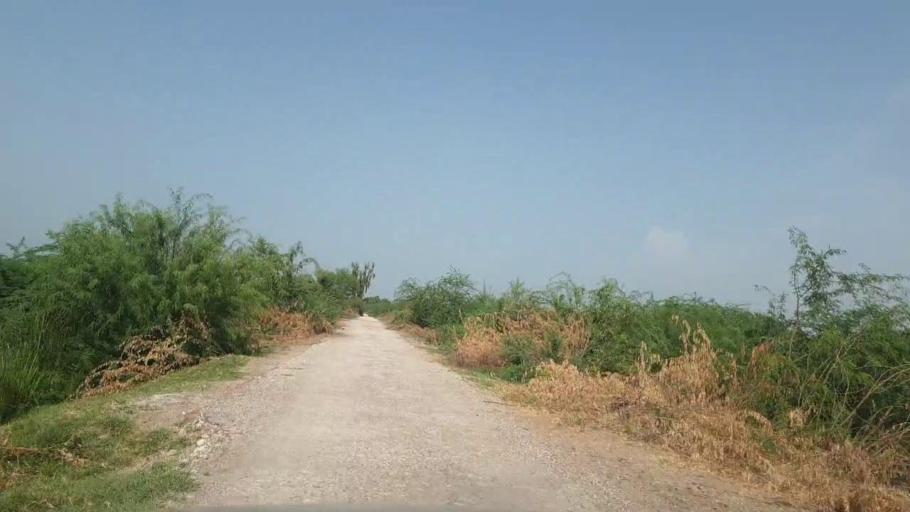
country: PK
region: Sindh
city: Pano Aqil
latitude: 27.7553
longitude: 69.1764
